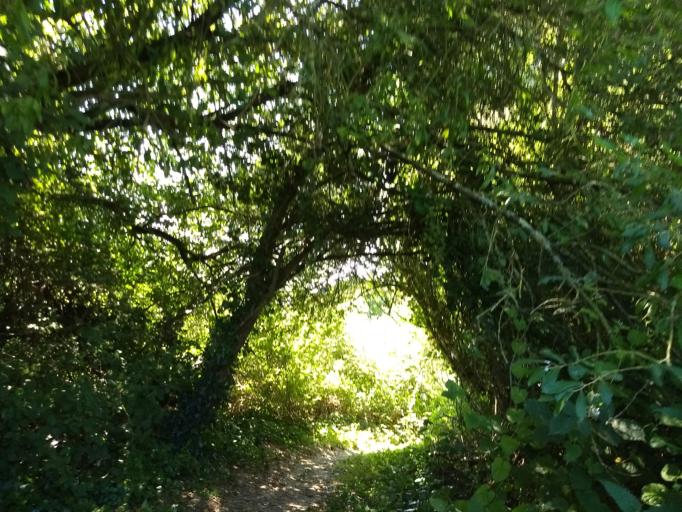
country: GB
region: England
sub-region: Isle of Wight
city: Newport
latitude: 50.7015
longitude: -1.3200
